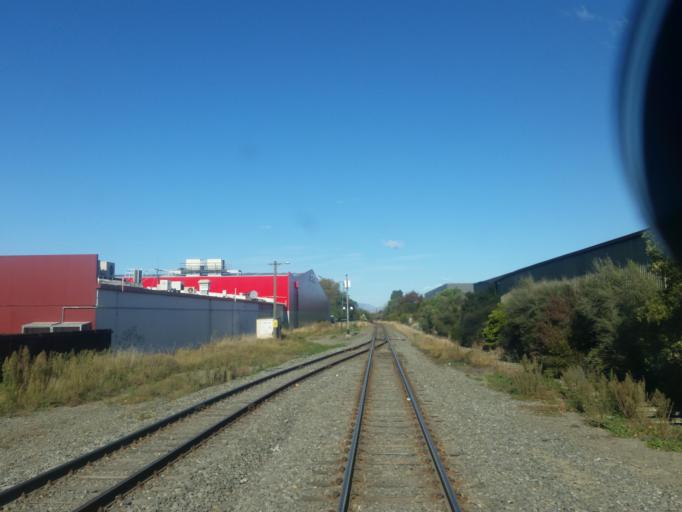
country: NZ
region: Canterbury
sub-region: Waimakariri District
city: Woodend
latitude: -43.3031
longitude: 172.5983
